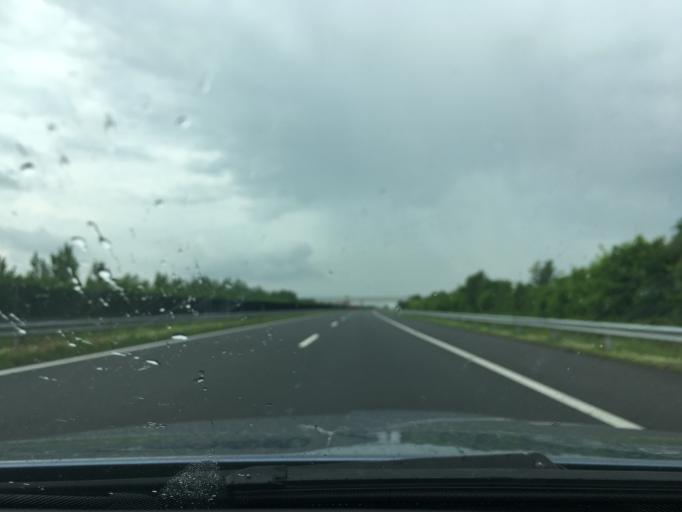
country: HU
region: Borsod-Abauj-Zemplen
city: Mezokeresztes
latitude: 47.8079
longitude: 20.6989
